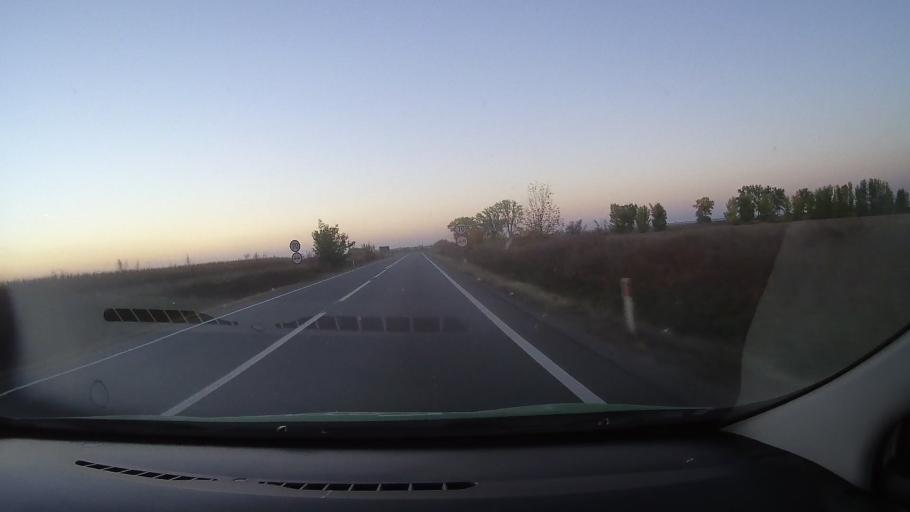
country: RO
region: Bihor
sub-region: Comuna Tarcea
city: Tarcea
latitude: 47.4326
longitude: 22.2055
